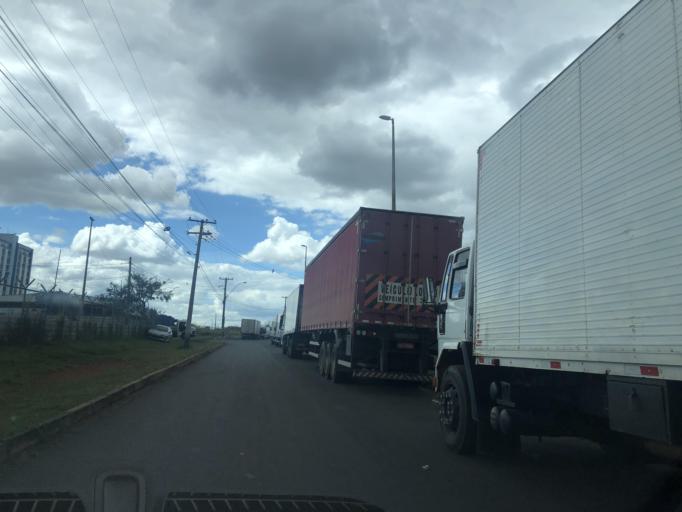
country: BR
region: Federal District
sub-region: Brasilia
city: Brasilia
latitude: -15.8742
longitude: -48.0271
